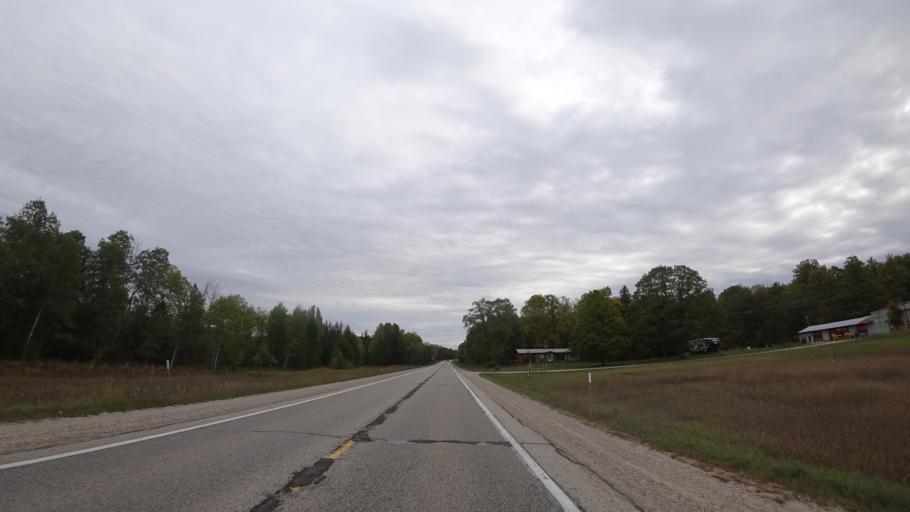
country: US
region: Michigan
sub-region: Charlevoix County
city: Boyne City
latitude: 45.2455
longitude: -84.9188
